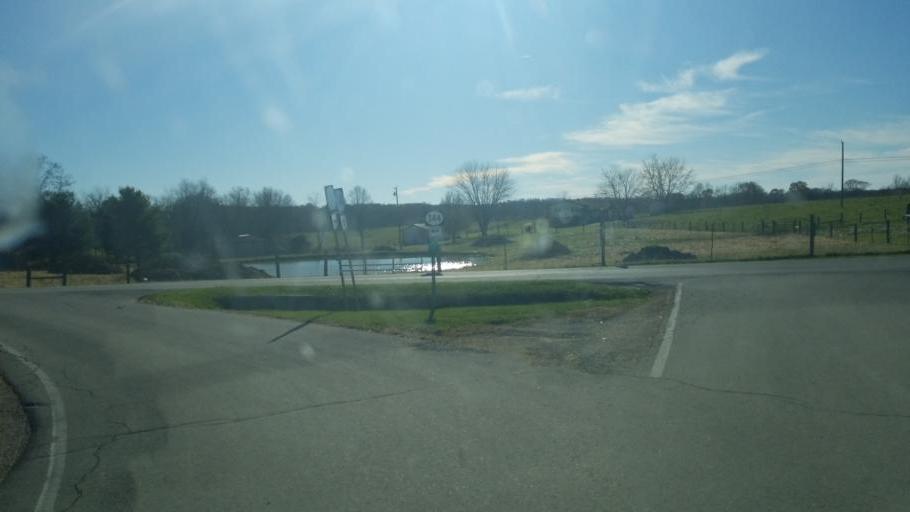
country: US
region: Kentucky
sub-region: Fleming County
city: Flemingsburg
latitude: 38.4606
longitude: -83.5242
